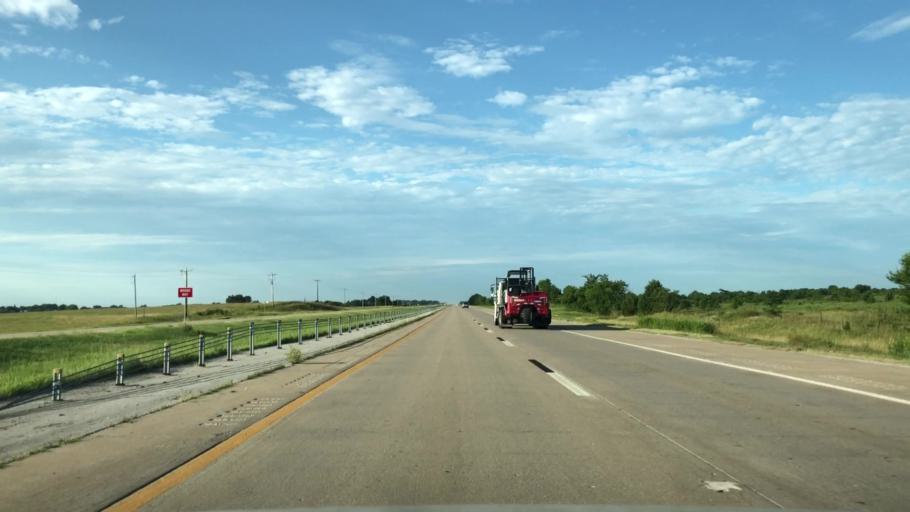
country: US
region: Oklahoma
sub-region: Osage County
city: Skiatook
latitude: 36.4525
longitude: -95.9206
